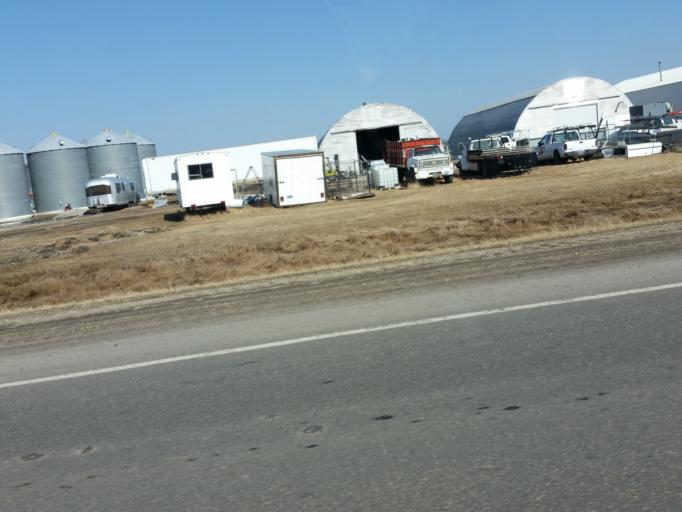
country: US
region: North Dakota
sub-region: Grand Forks County
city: Grand Forks
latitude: 48.0781
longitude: -97.1764
